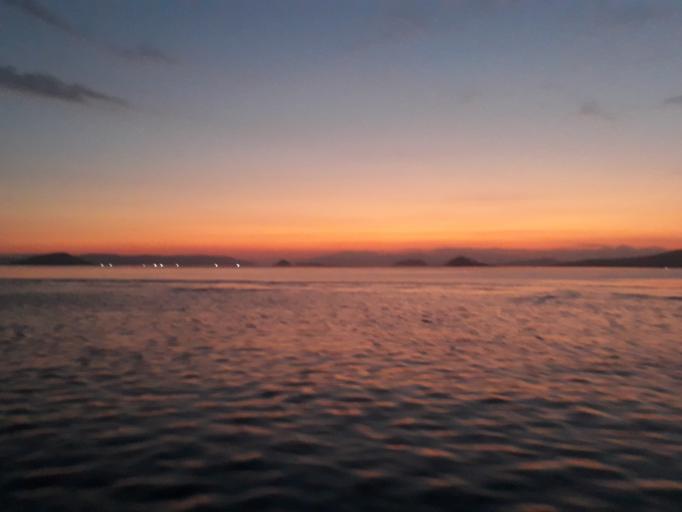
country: ID
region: East Nusa Tenggara
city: Kenari
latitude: -8.6017
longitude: 119.7665
